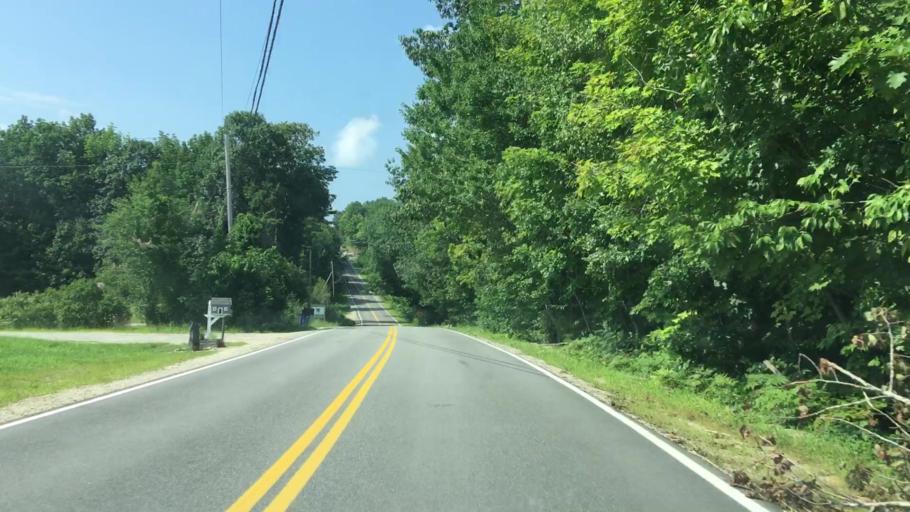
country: US
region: Maine
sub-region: Androscoggin County
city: Poland
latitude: 43.9830
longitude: -70.3987
